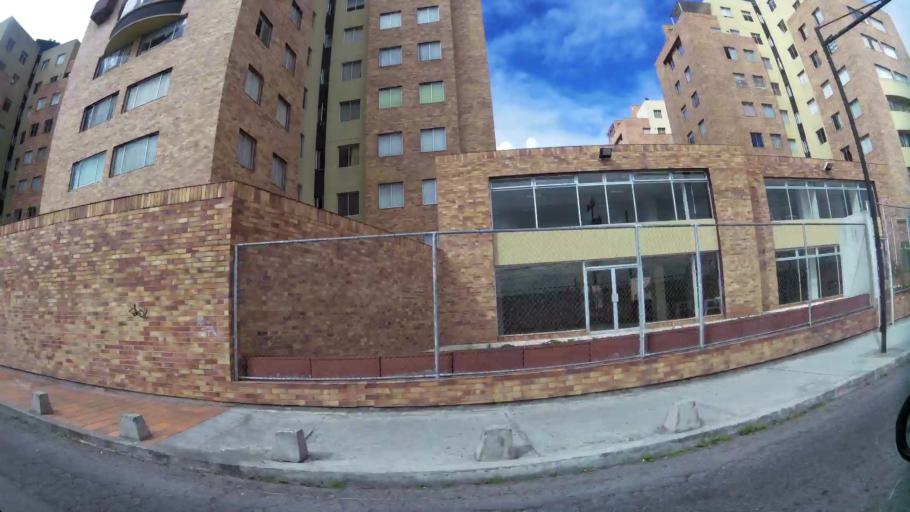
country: EC
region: Pichincha
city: Quito
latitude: -0.1692
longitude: -78.4771
